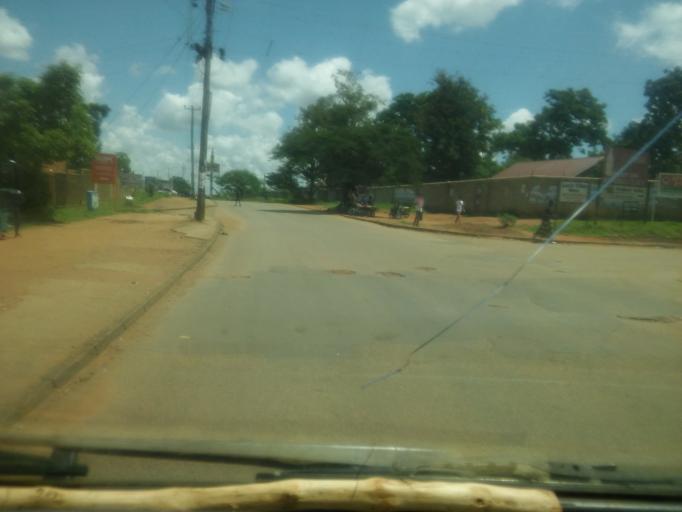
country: UG
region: Eastern Region
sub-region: Mbale District
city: Mbale
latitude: 1.0792
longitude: 34.1709
